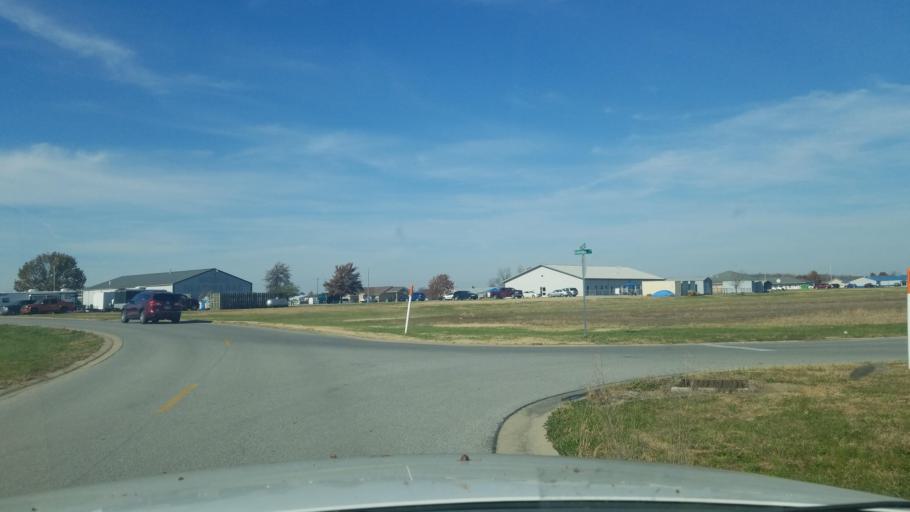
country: US
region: Illinois
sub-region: Saline County
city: Harrisburg
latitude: 37.7437
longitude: -88.5302
